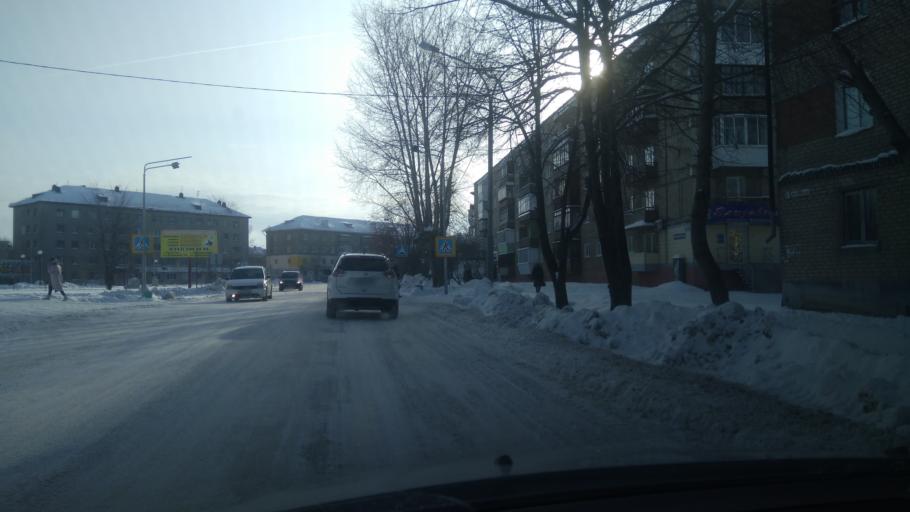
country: RU
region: Sverdlovsk
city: Sukhoy Log
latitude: 56.9096
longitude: 62.0333
